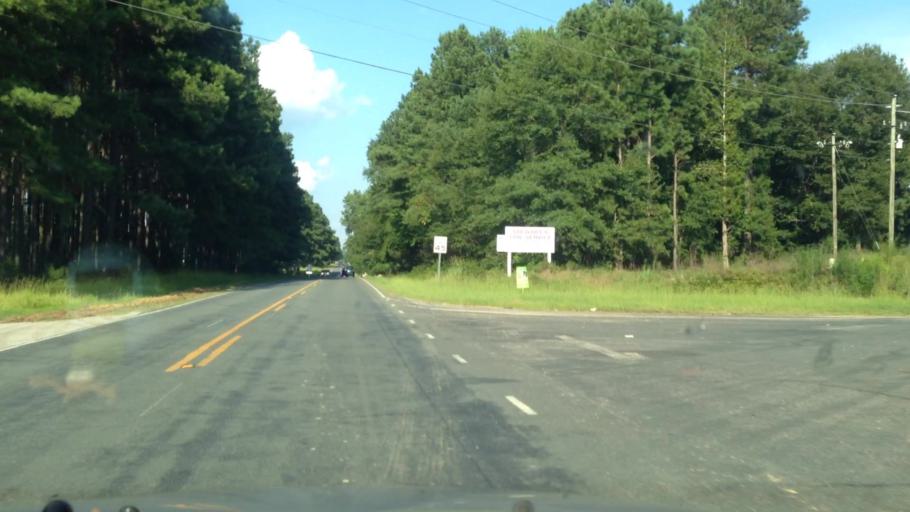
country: US
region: North Carolina
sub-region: Harnett County
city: Buies Creek
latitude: 35.4109
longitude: -78.7246
